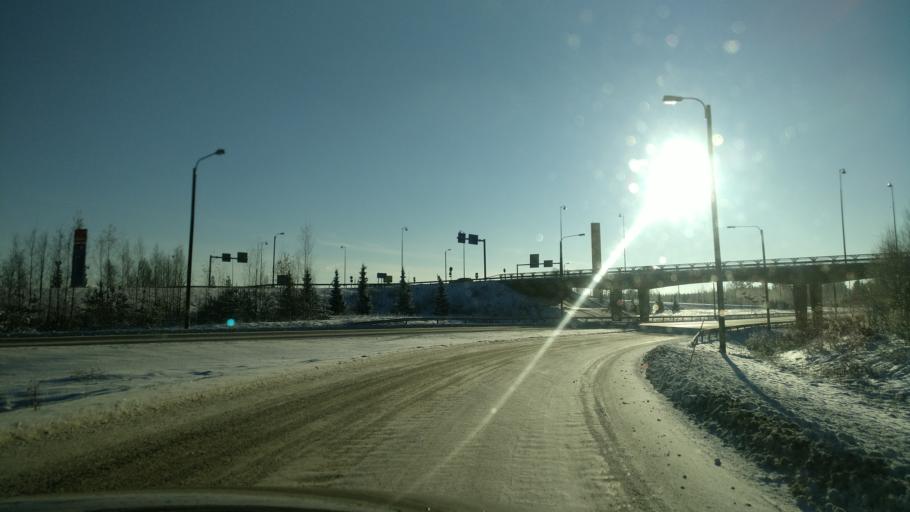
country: FI
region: Southern Savonia
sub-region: Pieksaemaeki
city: Juva
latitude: 61.8998
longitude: 27.8031
